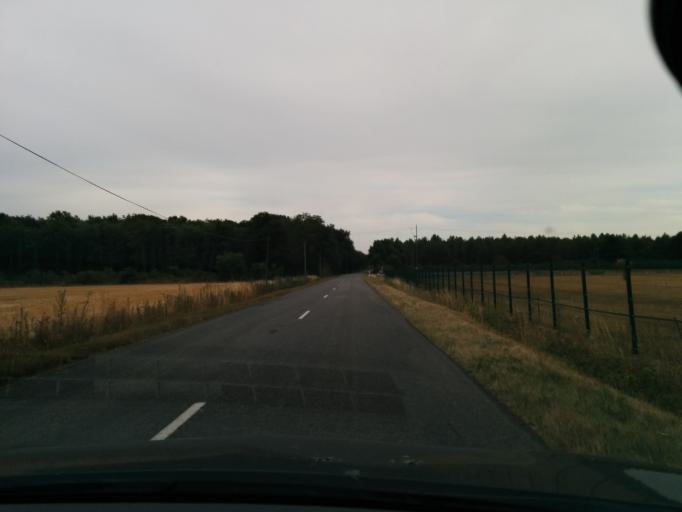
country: FR
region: Centre
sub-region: Departement du Loiret
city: Chateauneuf-sur-Loire
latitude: 47.8998
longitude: 2.1828
